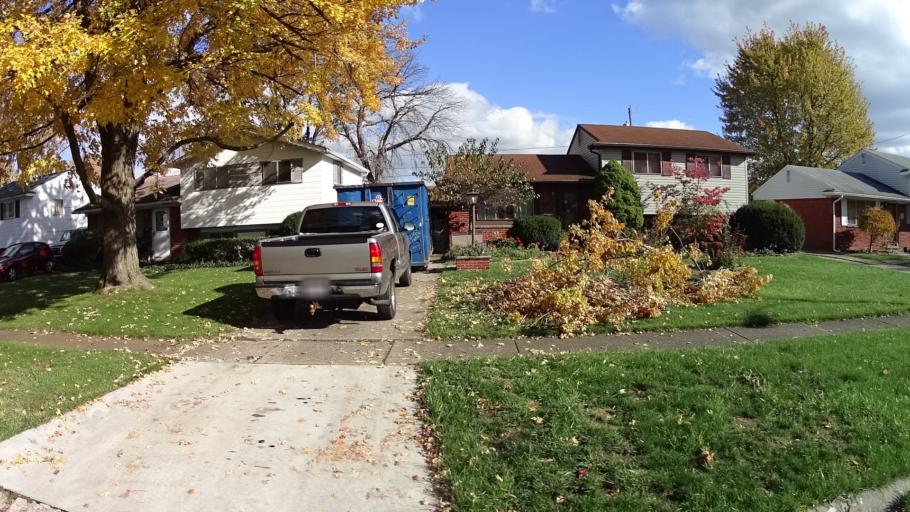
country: US
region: Ohio
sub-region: Lorain County
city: Sheffield
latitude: 41.4256
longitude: -82.1120
